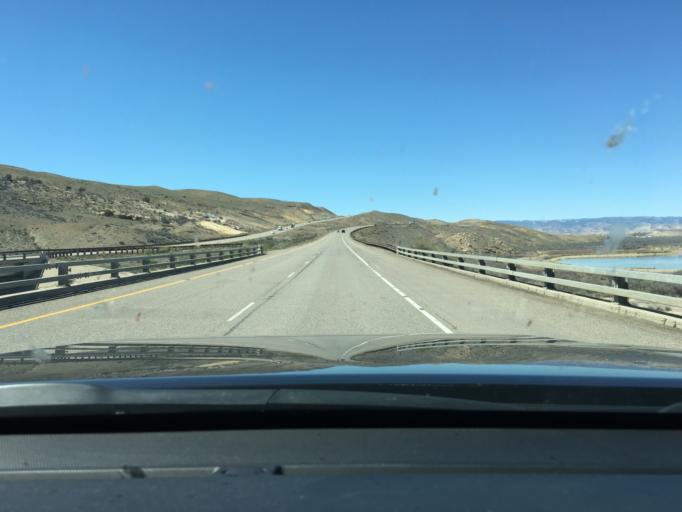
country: US
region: Colorado
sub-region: Mesa County
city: Loma
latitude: 39.2232
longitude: -108.8903
